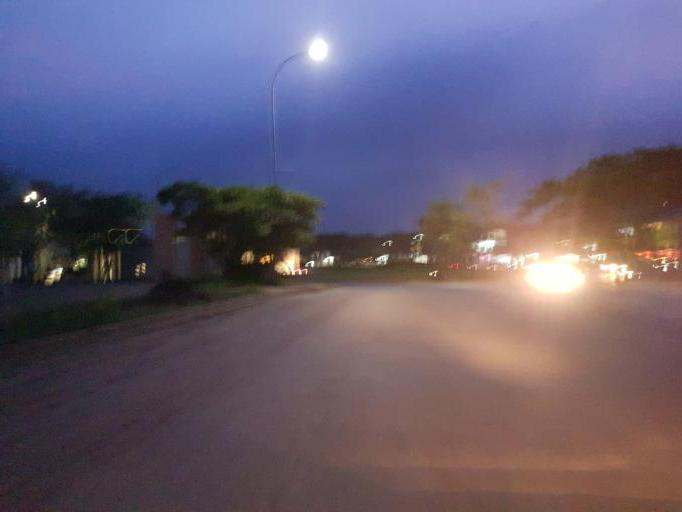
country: ID
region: West Java
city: Serpong
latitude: -6.3151
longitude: 106.6536
